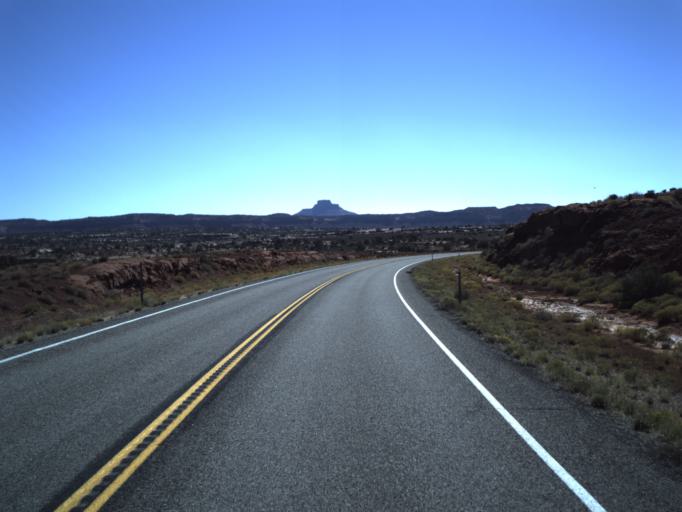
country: US
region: Utah
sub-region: San Juan County
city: Blanding
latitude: 37.8012
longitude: -110.3080
